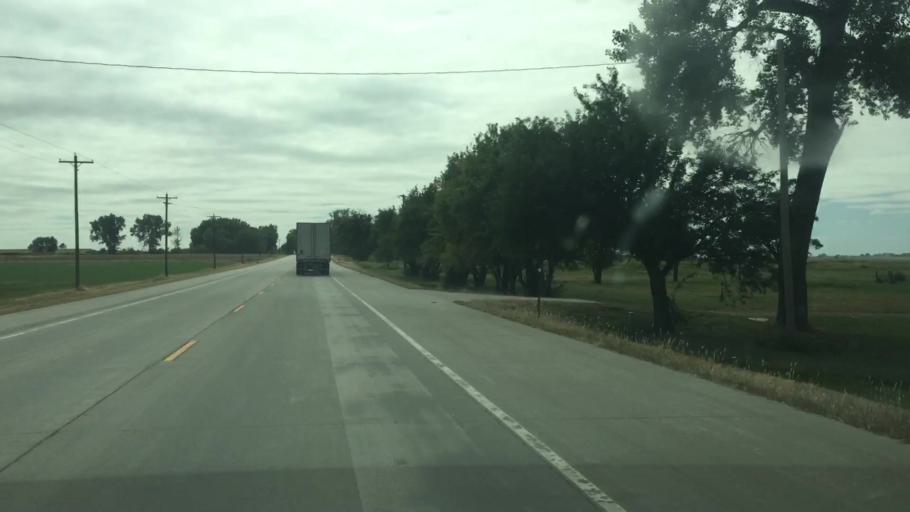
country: US
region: Colorado
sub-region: Prowers County
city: Lamar
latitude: 38.2138
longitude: -102.7241
